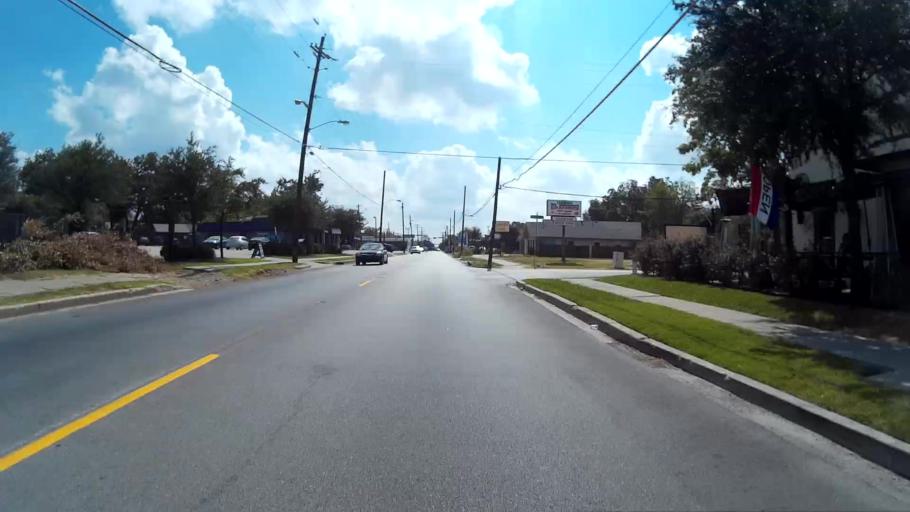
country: US
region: Texas
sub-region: Dallas County
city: Highland Park
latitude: 32.8130
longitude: -96.7764
